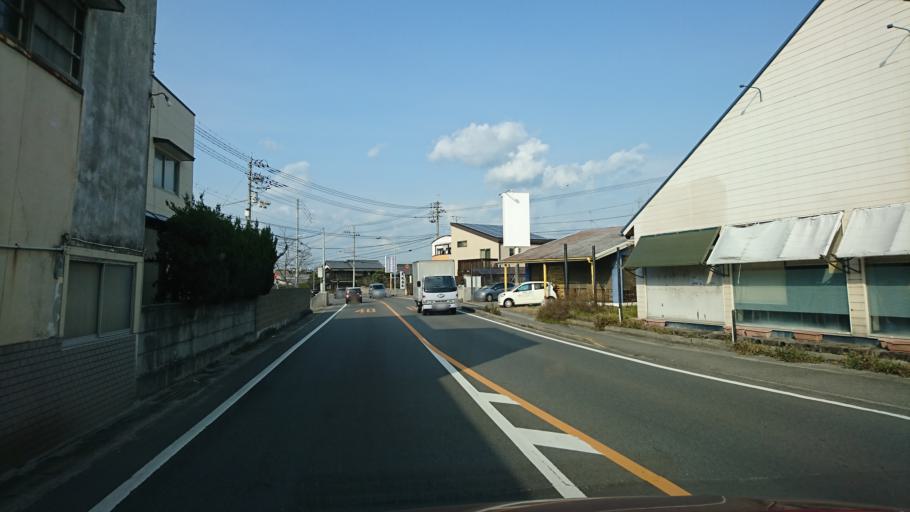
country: JP
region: Ehime
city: Saijo
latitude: 34.0261
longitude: 133.0381
